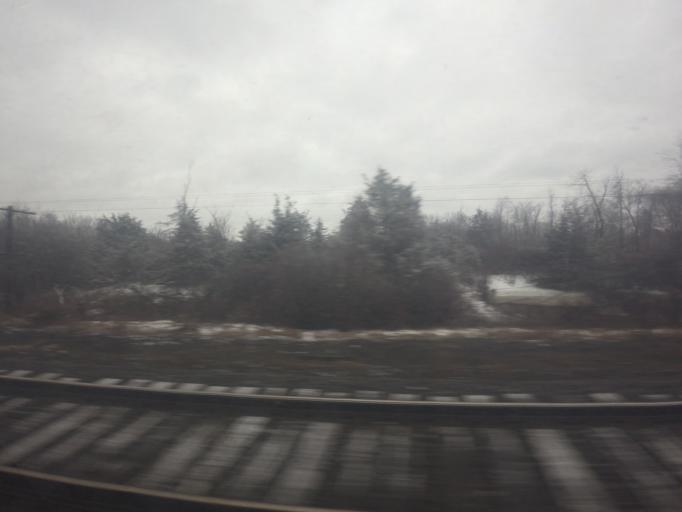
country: CA
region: Ontario
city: Gananoque
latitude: 44.3613
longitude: -76.1778
